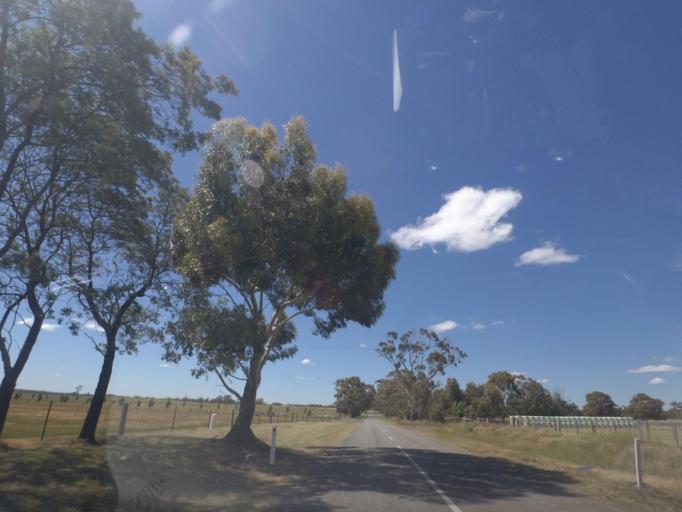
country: AU
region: Victoria
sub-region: Mount Alexander
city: Castlemaine
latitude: -37.3165
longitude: 144.4412
